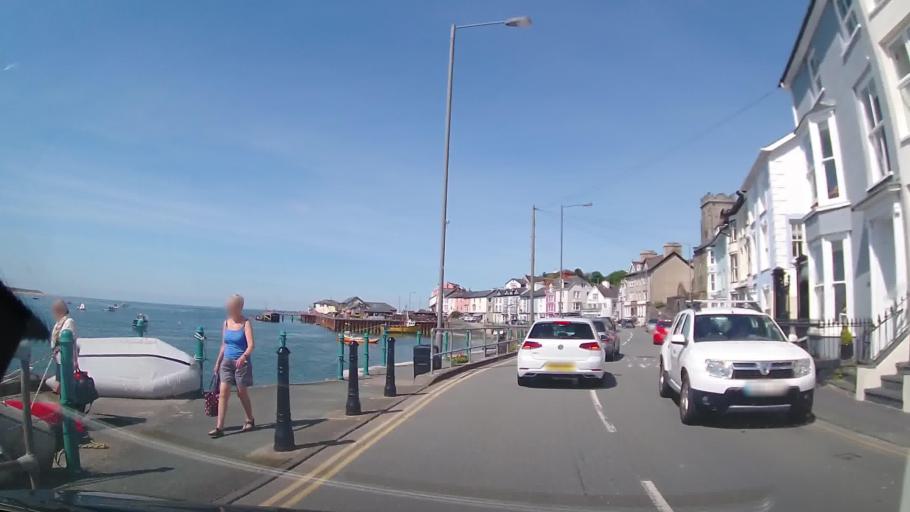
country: GB
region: Wales
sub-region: Gwynedd
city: Tywyn
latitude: 52.5441
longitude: -4.0419
